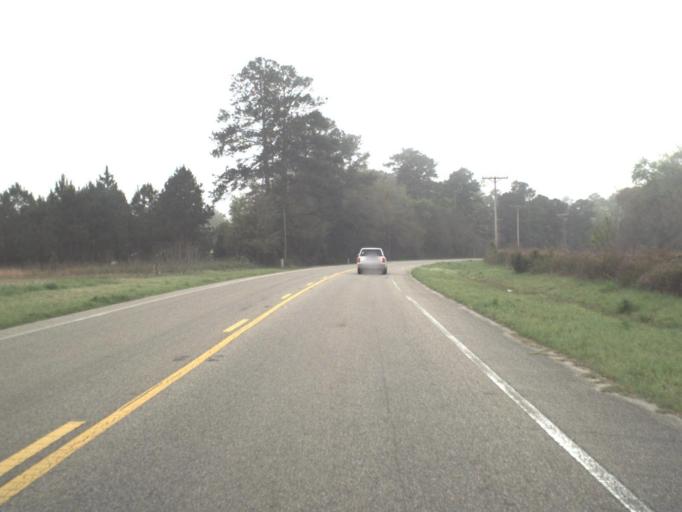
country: US
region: Florida
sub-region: Gadsden County
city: Gretna
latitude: 30.5434
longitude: -84.6769
